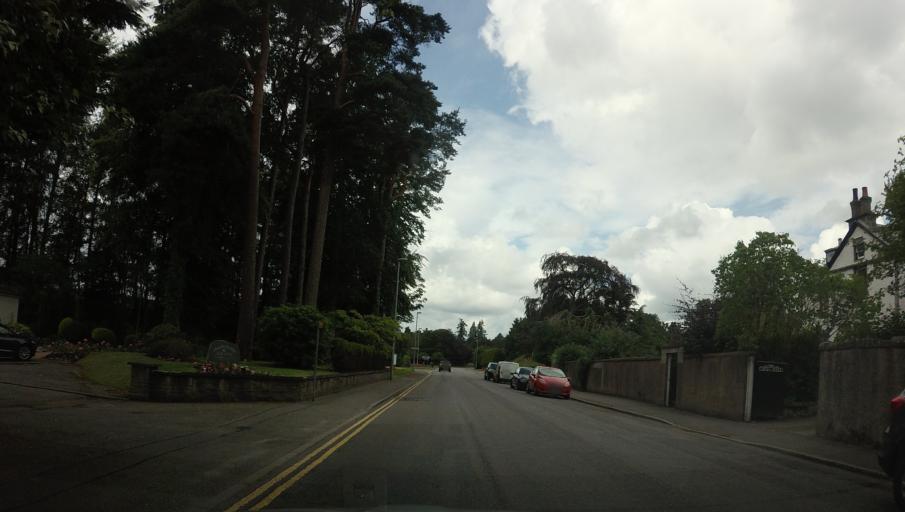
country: GB
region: Scotland
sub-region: Aberdeenshire
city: Banchory
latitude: 57.0517
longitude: -2.5082
